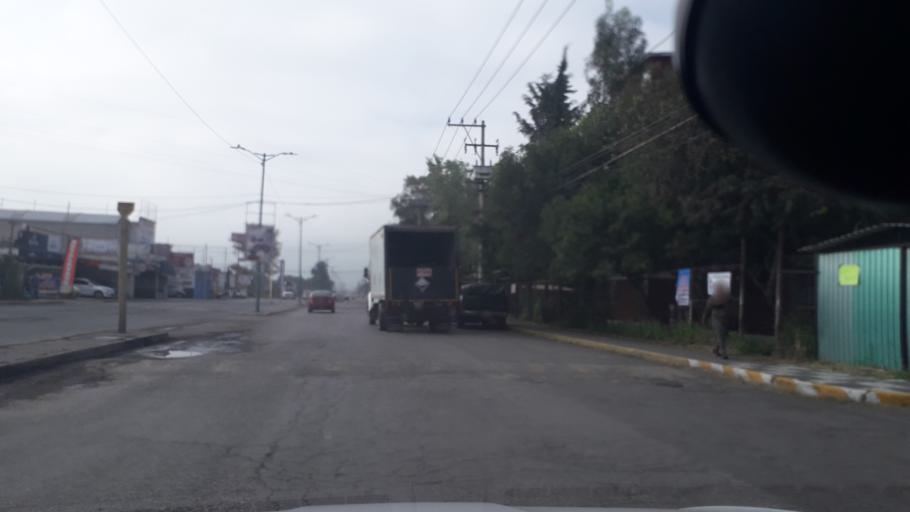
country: MX
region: Mexico
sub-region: Jaltenco
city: Alborada Jaltenco
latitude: 19.6516
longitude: -99.0769
